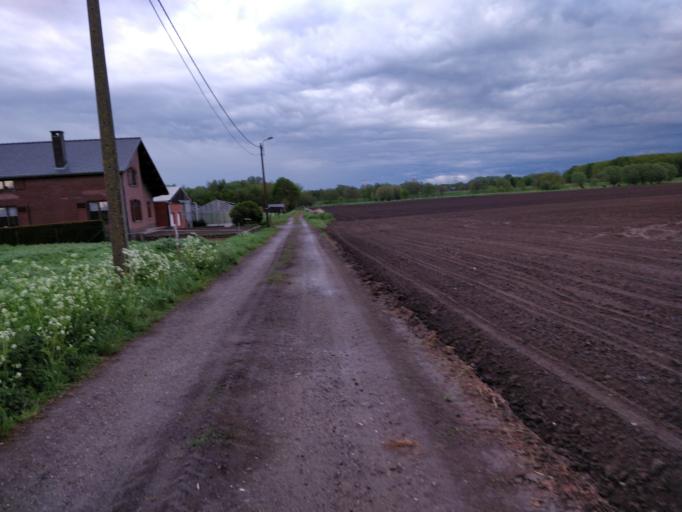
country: BE
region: Flanders
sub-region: Provincie Antwerpen
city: Mechelen
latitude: 51.0237
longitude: 4.4305
